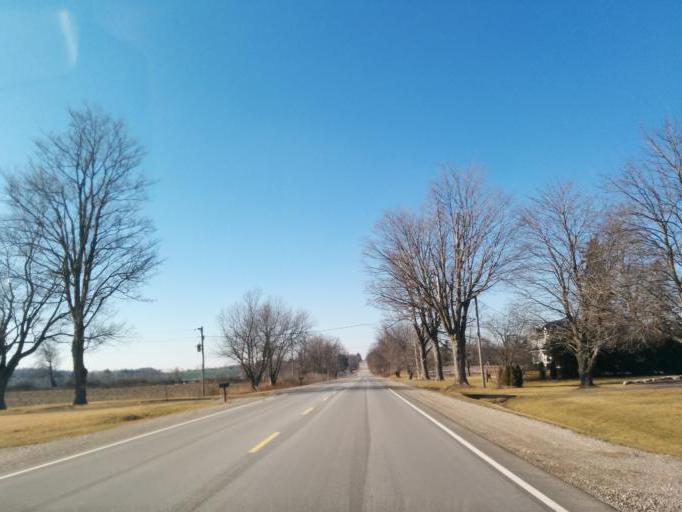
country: CA
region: Ontario
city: Brant
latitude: 43.0345
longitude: -80.3131
